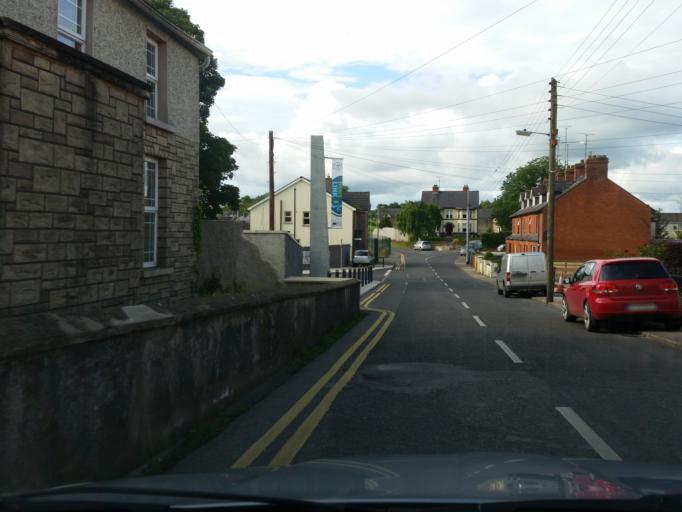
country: IE
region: Ulster
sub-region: County Monaghan
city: Clones
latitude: 54.1866
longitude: -7.2357
